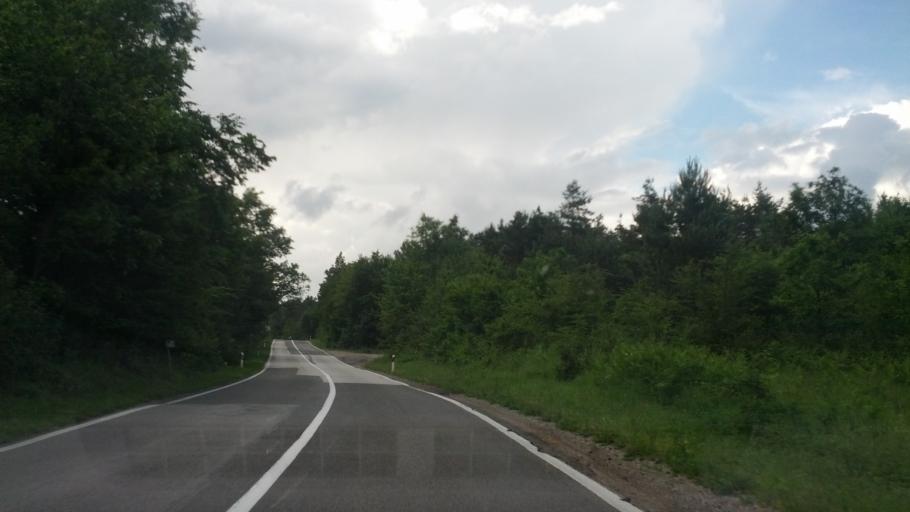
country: HR
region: Licko-Senjska
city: Jezerce
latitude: 44.9288
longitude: 15.7020
